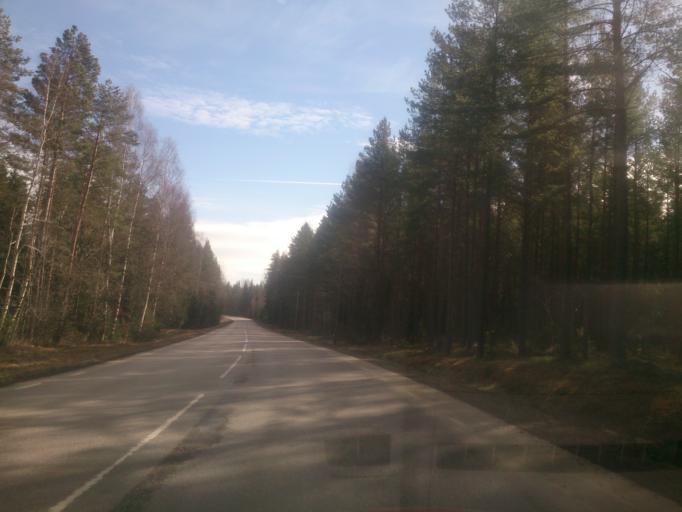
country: SE
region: OEstergoetland
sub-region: Finspangs Kommun
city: Finspang
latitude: 58.6592
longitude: 15.7840
